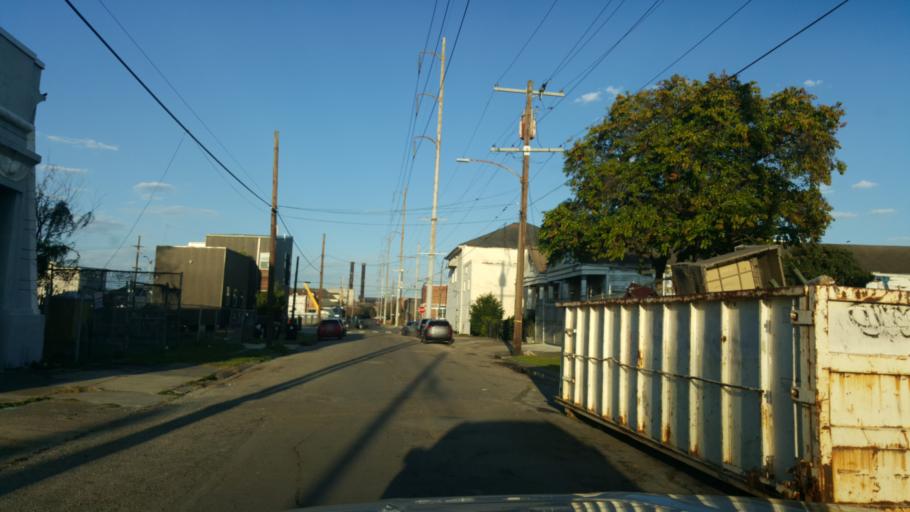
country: US
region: Louisiana
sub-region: Jefferson Parish
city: Harvey
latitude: 29.9242
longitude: -90.0734
